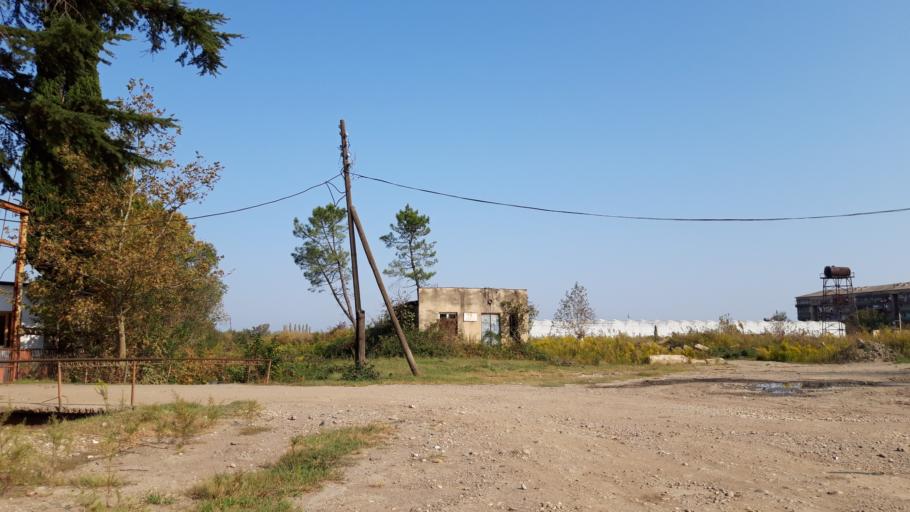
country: GE
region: Imereti
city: Samtredia
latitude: 42.1637
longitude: 42.3270
